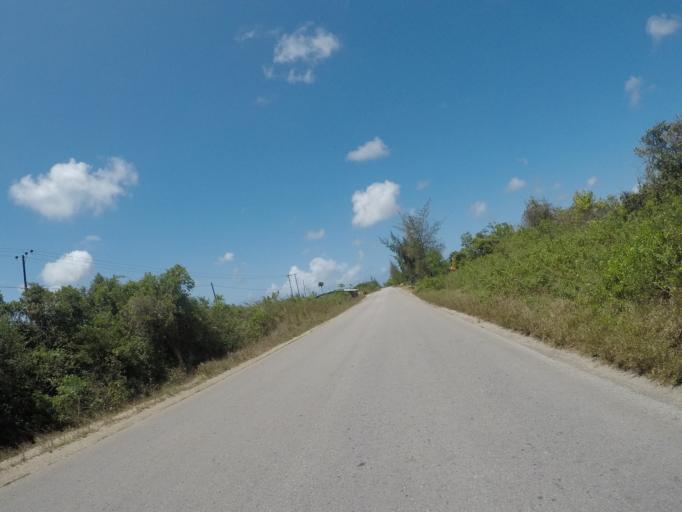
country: TZ
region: Zanzibar Central/South
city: Nganane
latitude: -6.2830
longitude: 39.4674
